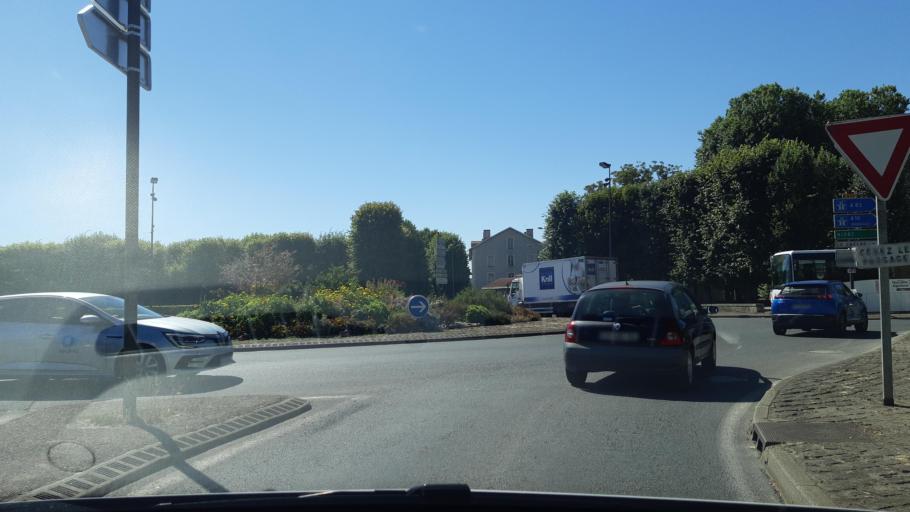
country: FR
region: Poitou-Charentes
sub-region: Departement des Deux-Sevres
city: Exireuil
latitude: 46.4152
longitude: -0.2011
